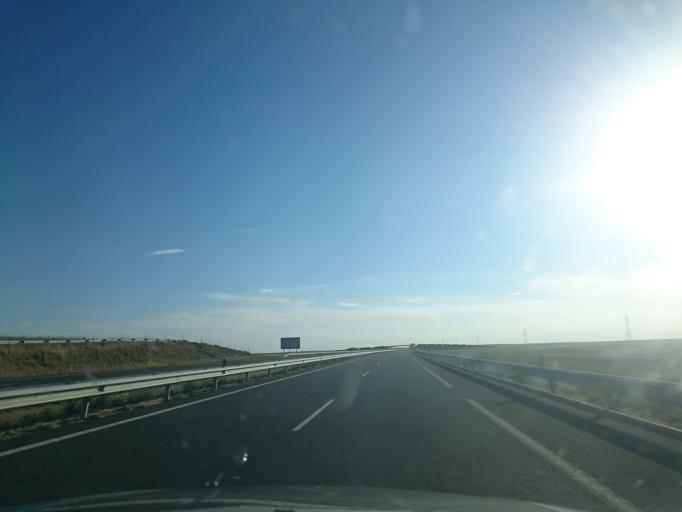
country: ES
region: Castille and Leon
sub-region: Provincia de Palencia
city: Villaherreros
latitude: 42.3858
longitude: -4.4875
